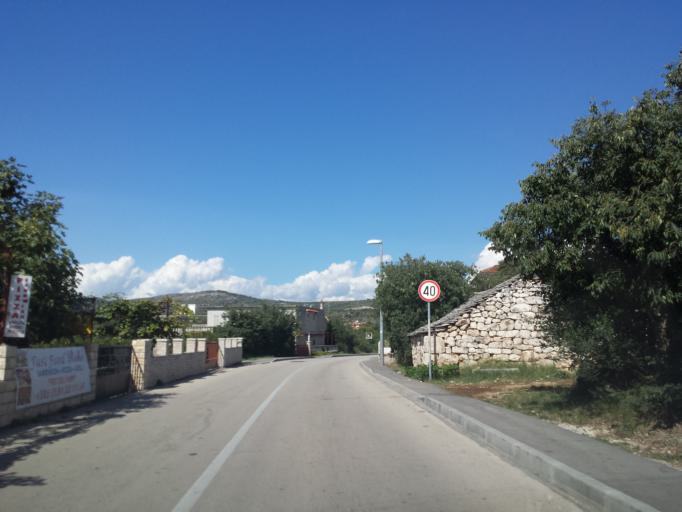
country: HR
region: Sibensko-Kniniska
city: Rogoznica
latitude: 43.5362
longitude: 15.9669
